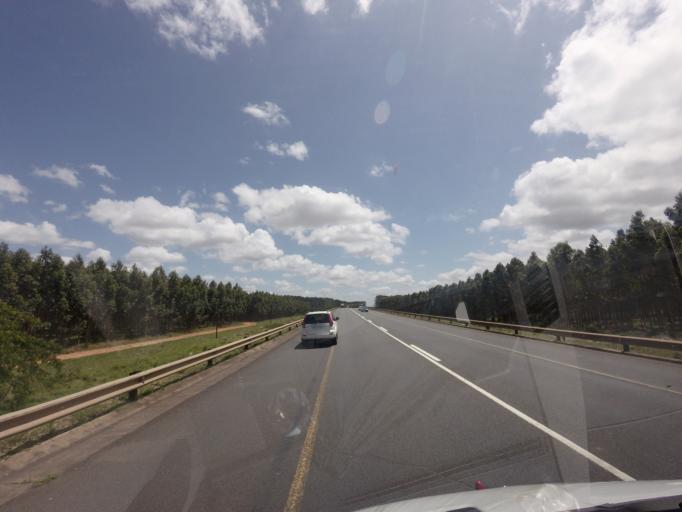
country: ZA
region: KwaZulu-Natal
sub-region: uThungulu District Municipality
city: KwaMbonambi
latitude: -28.5864
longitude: 32.0992
